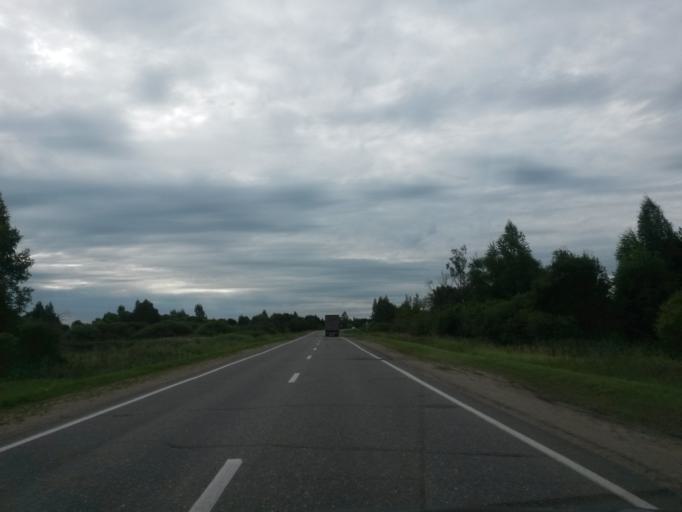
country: RU
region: Jaroslavl
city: Krasnyye Tkachi
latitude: 57.3730
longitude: 39.7280
